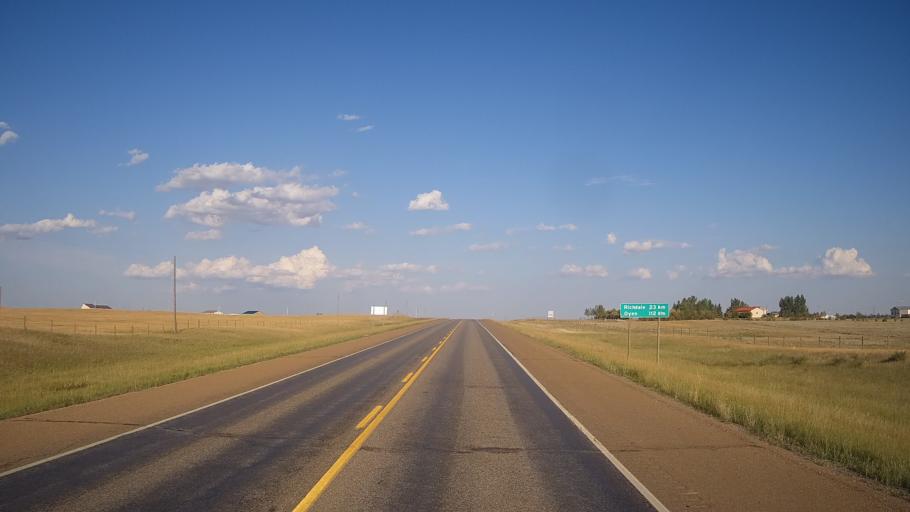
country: CA
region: Alberta
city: Hanna
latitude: 51.6299
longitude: -111.9147
